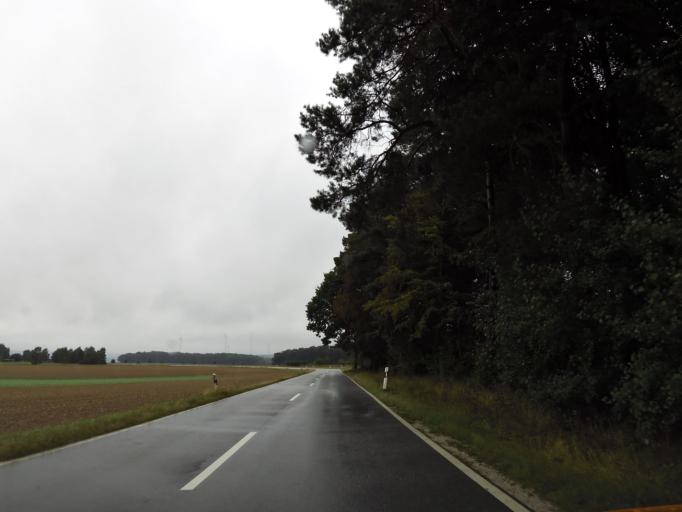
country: DE
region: Rheinland-Pfalz
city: Schnorbach
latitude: 49.9911
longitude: 7.6208
